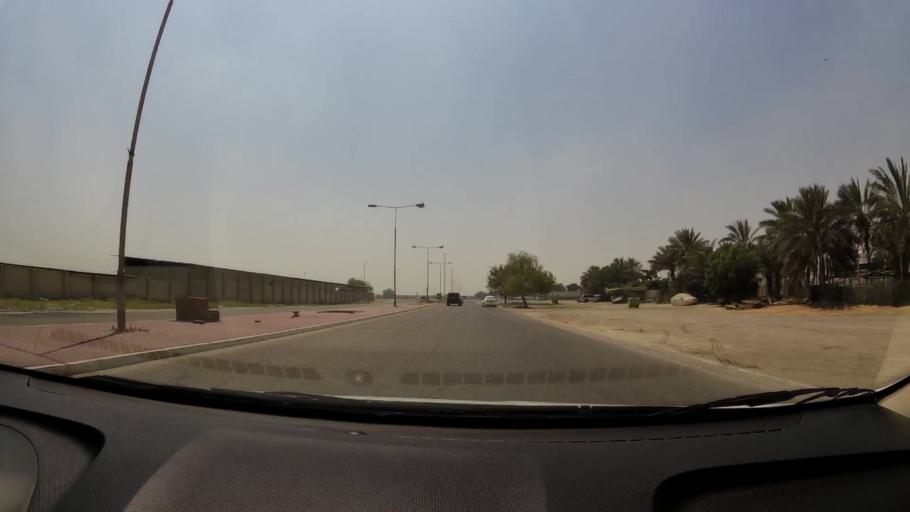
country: AE
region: Umm al Qaywayn
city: Umm al Qaywayn
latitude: 25.5633
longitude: 55.5584
